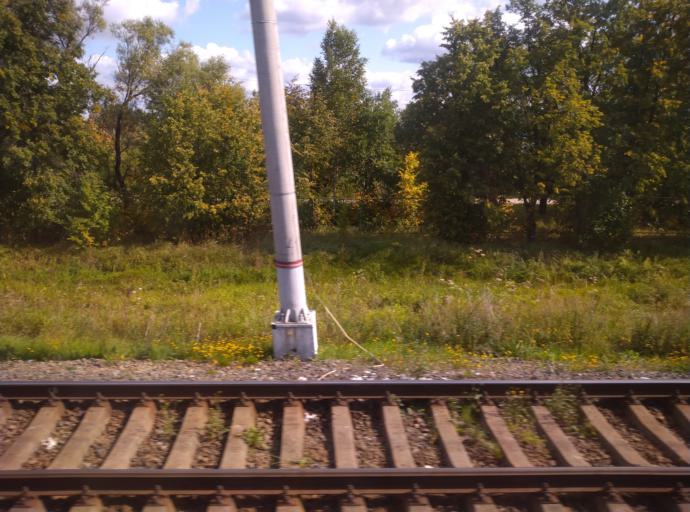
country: RU
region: Leningrad
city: Ul'yanovka
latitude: 59.6317
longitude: 30.7626
